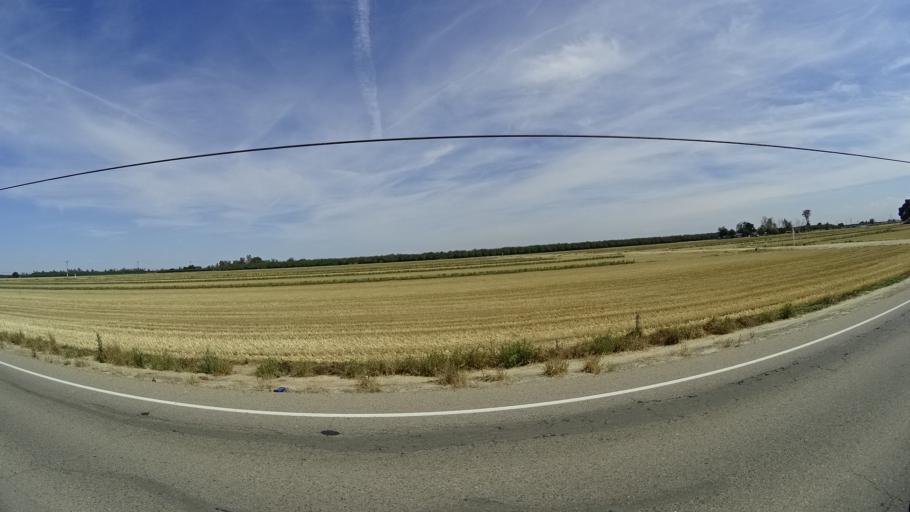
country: US
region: California
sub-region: Kings County
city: Hanford
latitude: 36.3425
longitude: -119.6075
